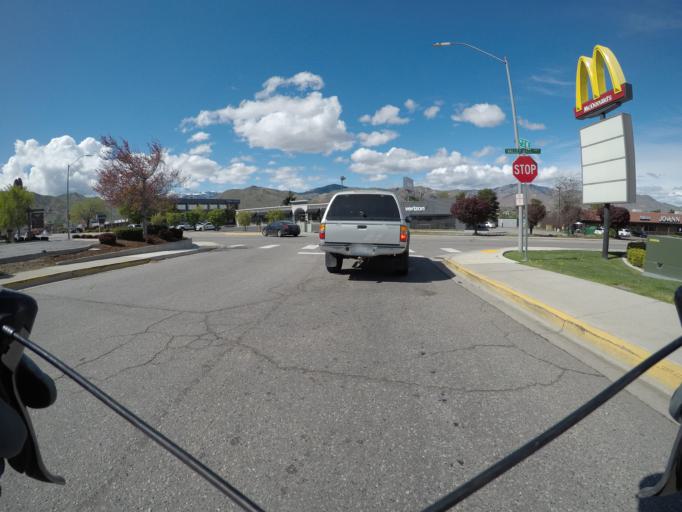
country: US
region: Washington
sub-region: Douglas County
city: East Wenatchee
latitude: 47.4078
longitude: -120.2882
